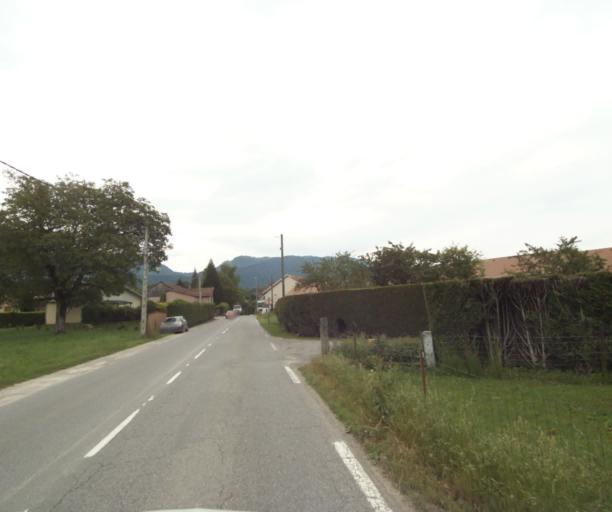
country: FR
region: Rhone-Alpes
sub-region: Departement de la Haute-Savoie
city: Allinges
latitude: 46.3365
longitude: 6.4784
